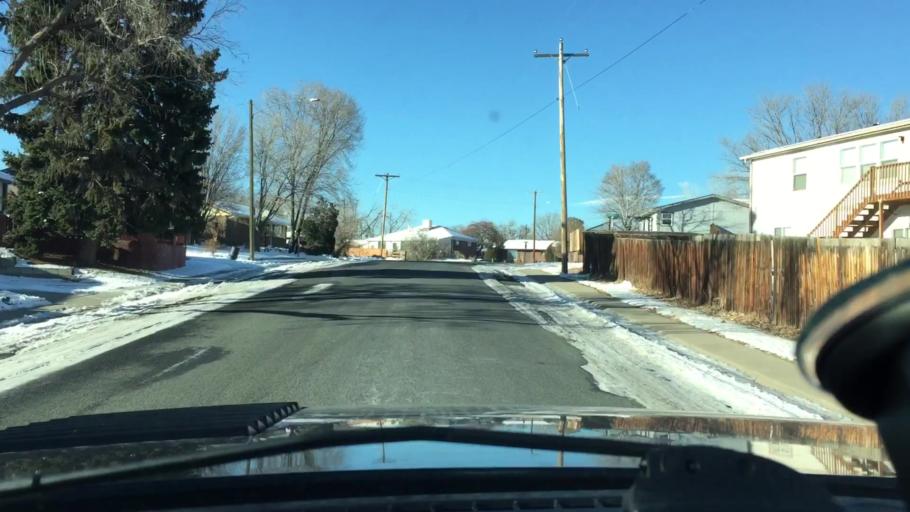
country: US
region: Colorado
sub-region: Adams County
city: Sherrelwood
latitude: 39.8385
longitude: -105.0027
